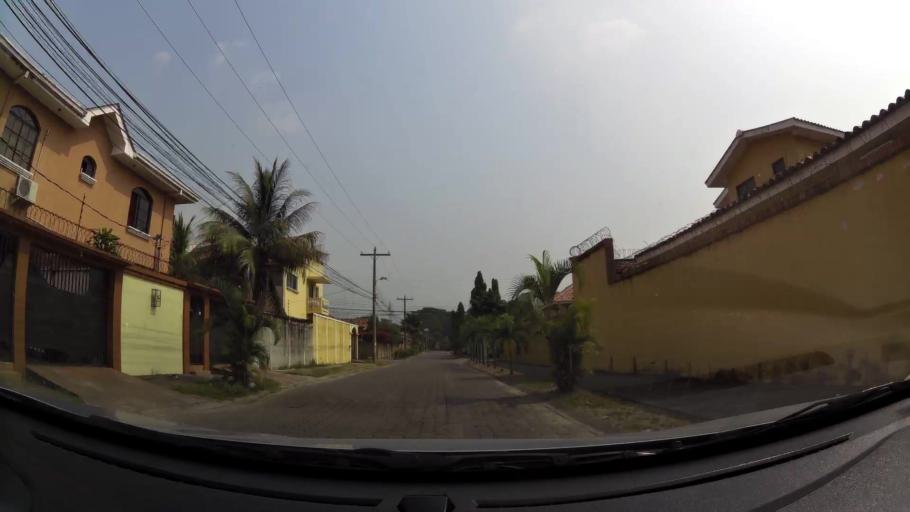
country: HN
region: Cortes
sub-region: San Pedro Sula
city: Pena Blanca
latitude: 15.5362
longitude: -88.0310
